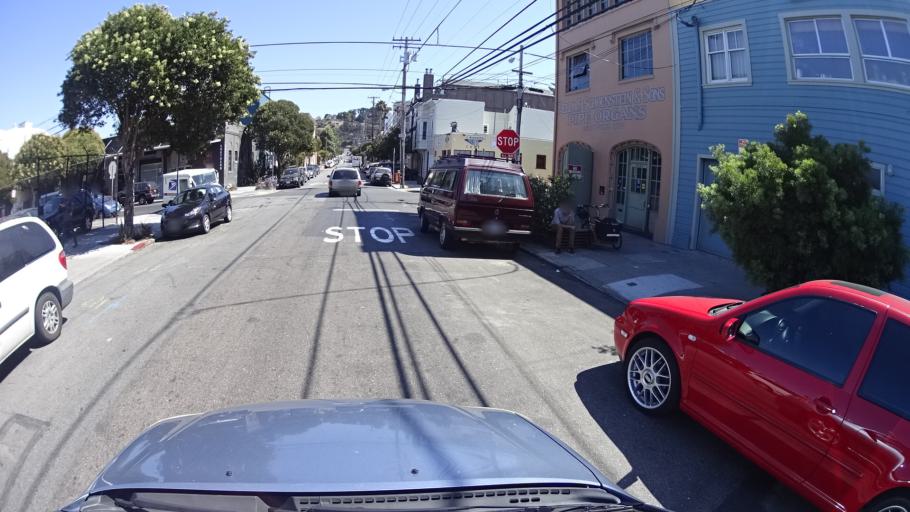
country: US
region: California
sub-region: San Francisco County
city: San Francisco
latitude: 37.7591
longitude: -122.4120
